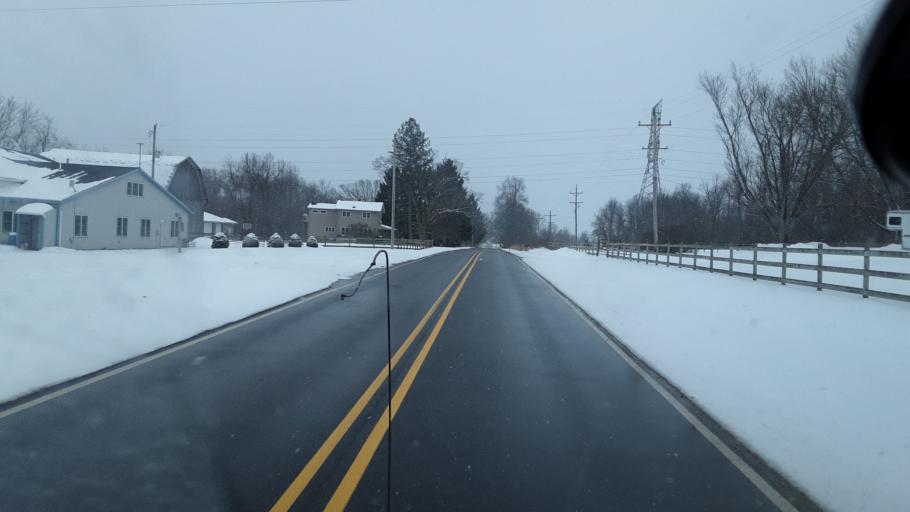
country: US
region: Michigan
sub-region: Ingham County
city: Leslie
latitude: 42.4177
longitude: -84.4433
